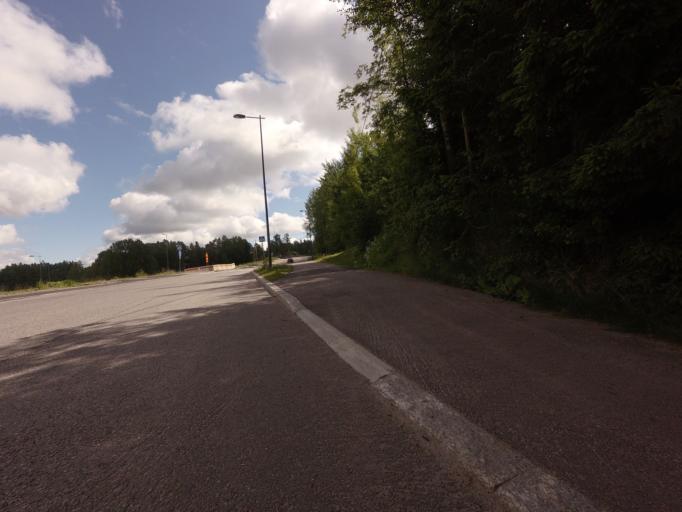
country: FI
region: Uusimaa
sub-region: Helsinki
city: Espoo
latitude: 60.1685
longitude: 24.6008
